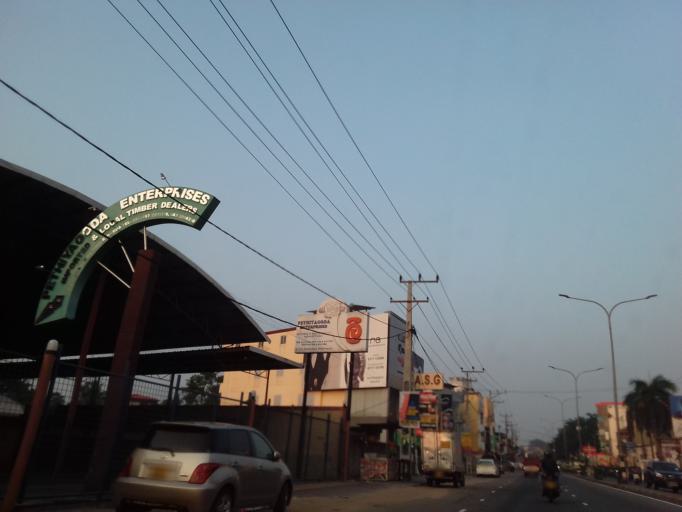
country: LK
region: Western
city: Kelaniya
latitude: 6.9832
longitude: 79.9319
